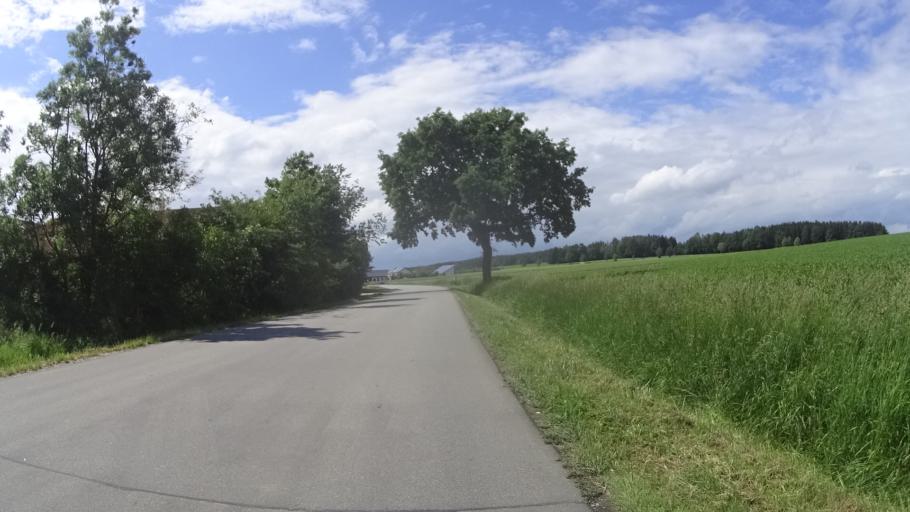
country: DE
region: Bavaria
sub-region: Lower Bavaria
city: Gangkofen
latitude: 48.4440
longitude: 12.5366
